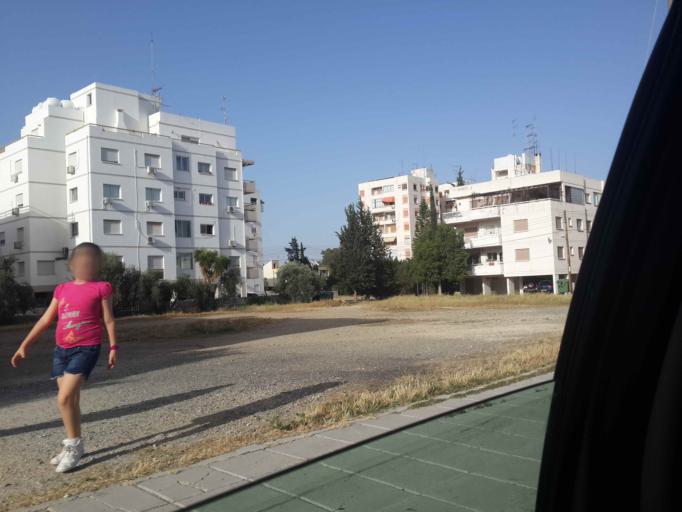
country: CY
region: Lefkosia
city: Nicosia
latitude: 35.1568
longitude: 33.3429
